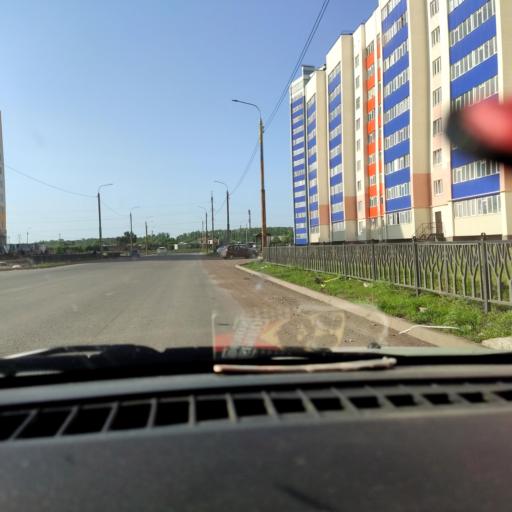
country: RU
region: Bashkortostan
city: Sterlitamak
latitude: 53.6375
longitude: 55.8934
